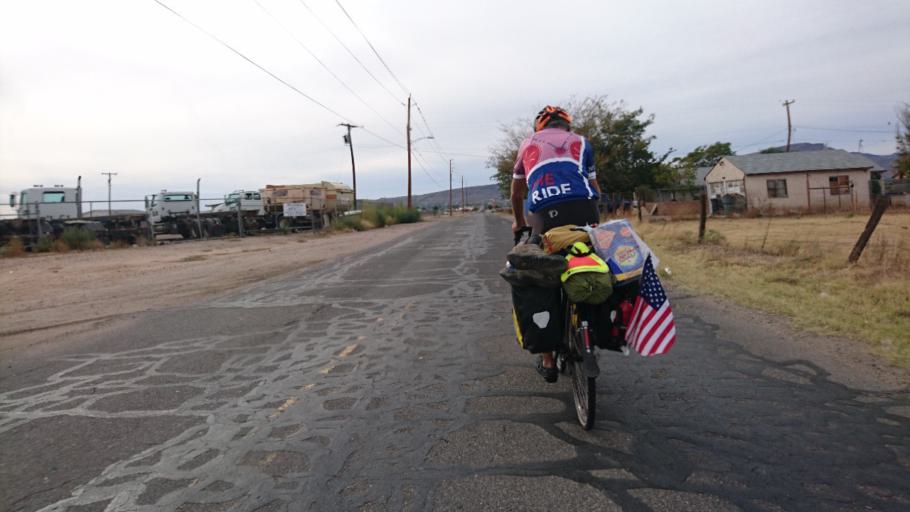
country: US
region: Arizona
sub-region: Mohave County
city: New Kingman-Butler
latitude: 35.2394
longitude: -113.9911
